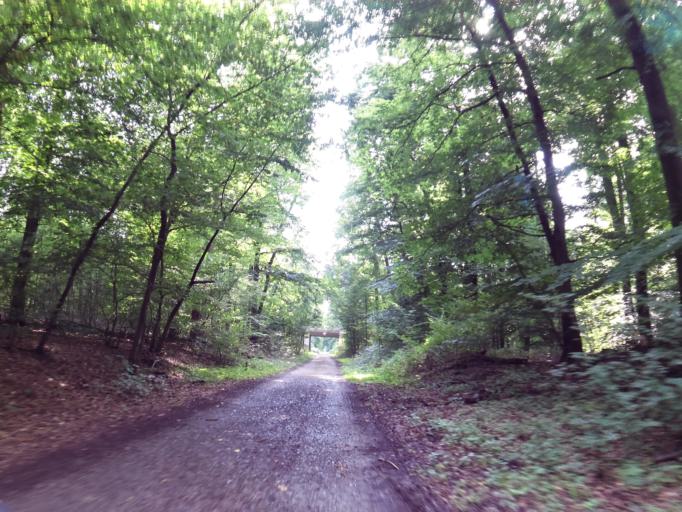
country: DE
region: Hesse
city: Morfelden-Walldorf
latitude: 50.0312
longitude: 8.6108
